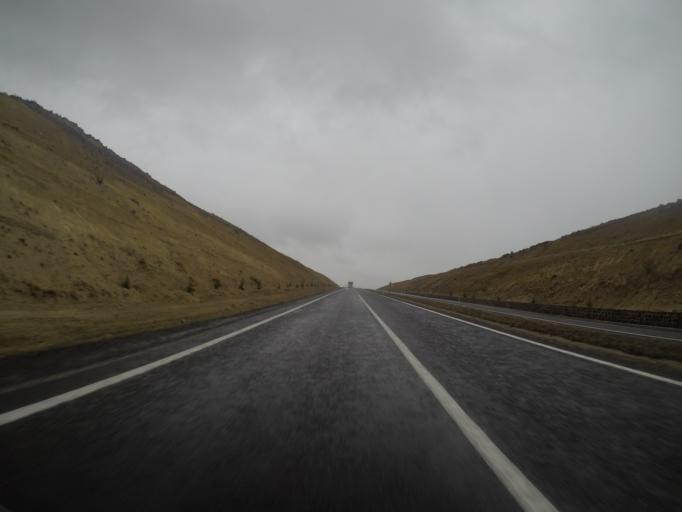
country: TR
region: Nevsehir
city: Urgub
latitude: 38.7418
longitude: 35.0124
